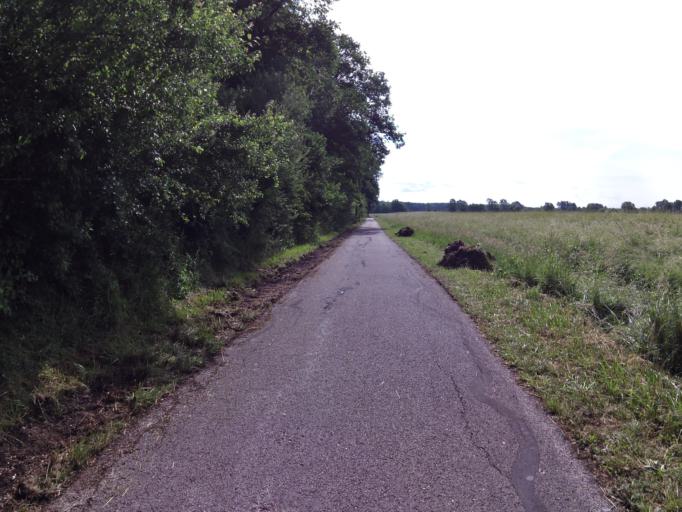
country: FR
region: Champagne-Ardenne
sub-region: Departement de l'Aube
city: Verrieres
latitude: 48.2640
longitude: 4.1848
